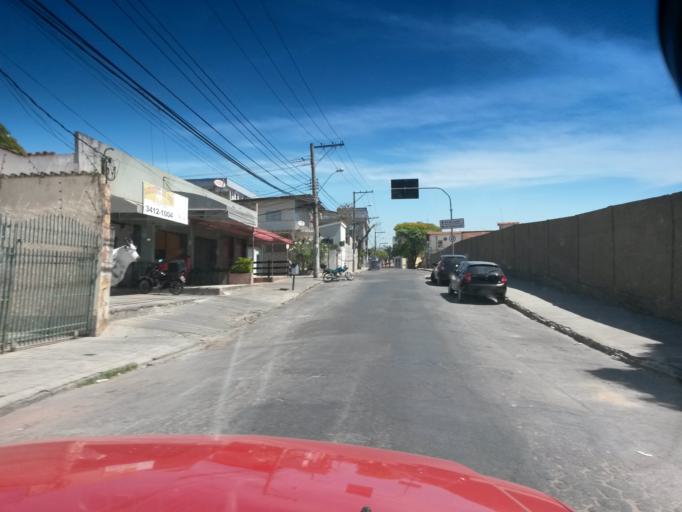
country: BR
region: Minas Gerais
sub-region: Belo Horizonte
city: Belo Horizonte
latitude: -19.9013
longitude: -43.9708
